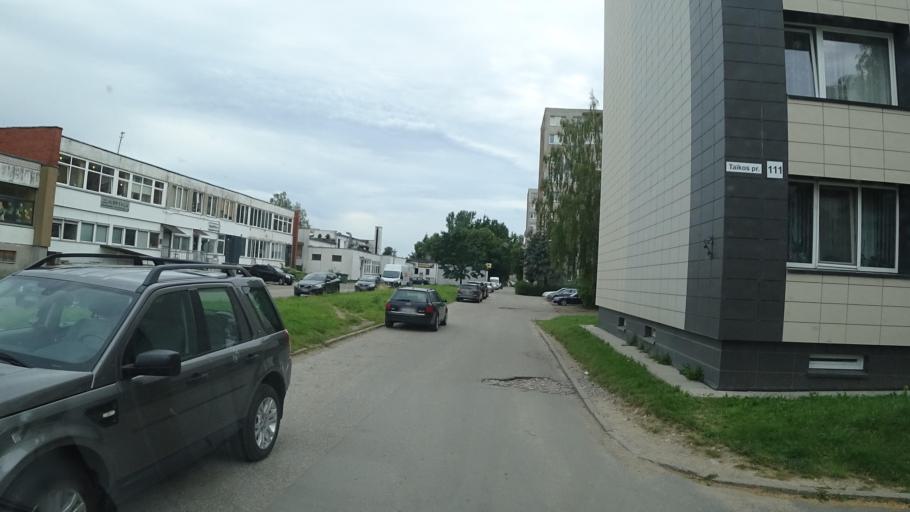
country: LT
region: Kauno apskritis
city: Dainava (Kaunas)
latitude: 54.9169
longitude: 23.9817
